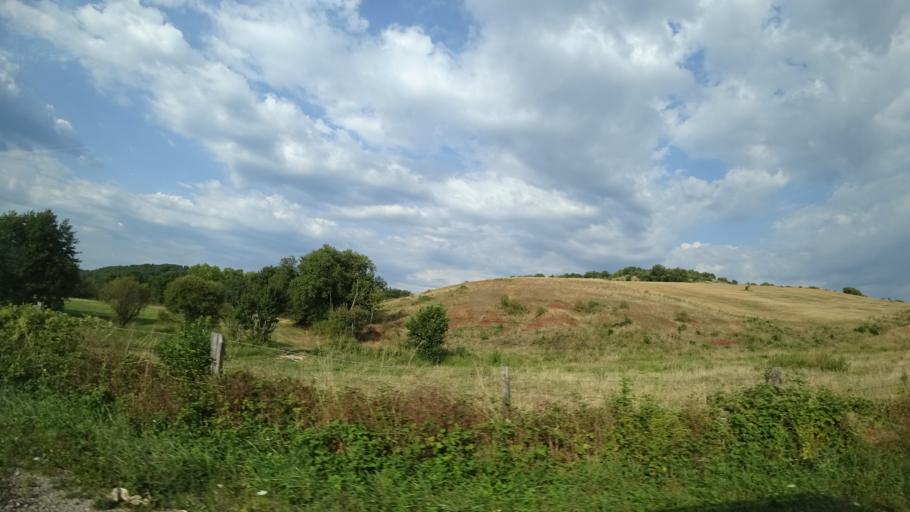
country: FR
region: Midi-Pyrenees
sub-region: Departement de l'Aveyron
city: Saint-Christophe-Vallon
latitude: 44.4912
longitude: 2.3888
